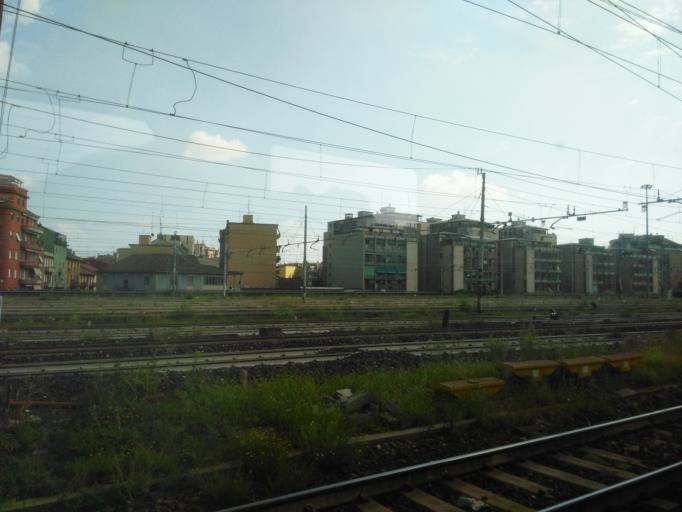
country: IT
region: Lombardy
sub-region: Citta metropolitana di Milano
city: Milano
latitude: 45.4954
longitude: 9.2139
